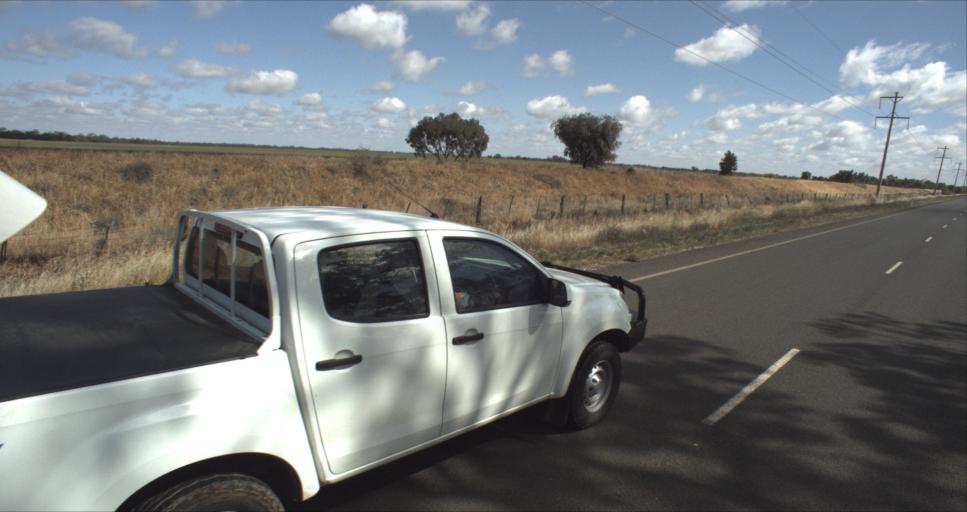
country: AU
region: New South Wales
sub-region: Murrumbidgee Shire
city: Darlington Point
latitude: -34.5388
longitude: 146.1725
